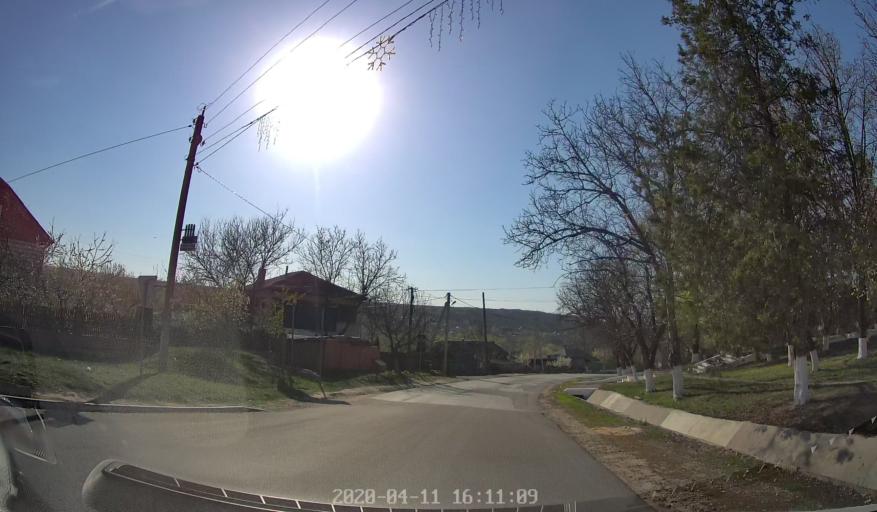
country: MD
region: Chisinau
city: Vadul lui Voda
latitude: 47.0683
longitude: 29.1286
